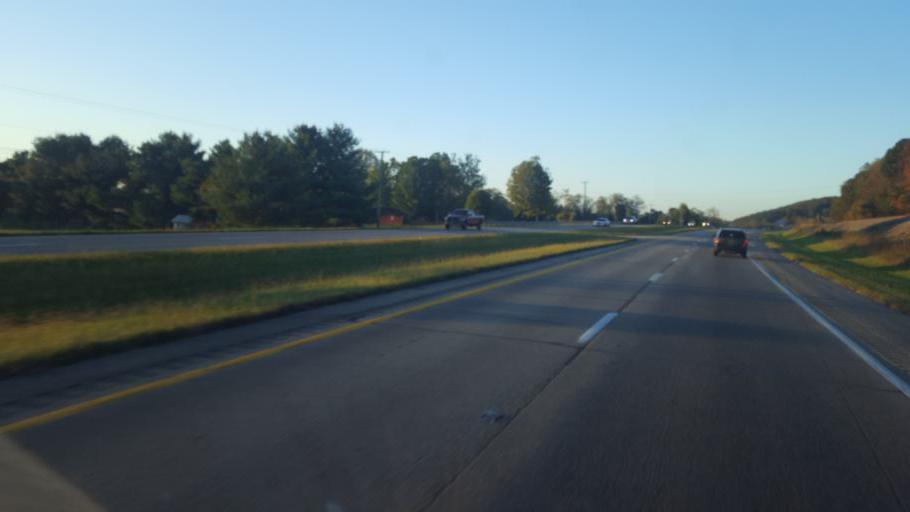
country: US
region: Ohio
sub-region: Scioto County
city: Lucasville
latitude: 38.9445
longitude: -83.0234
